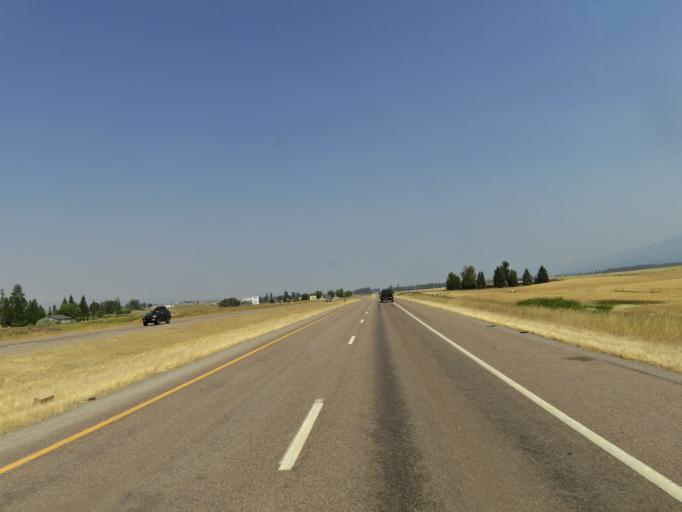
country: US
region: Montana
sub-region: Lake County
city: Pablo
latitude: 47.5659
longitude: -114.1129
